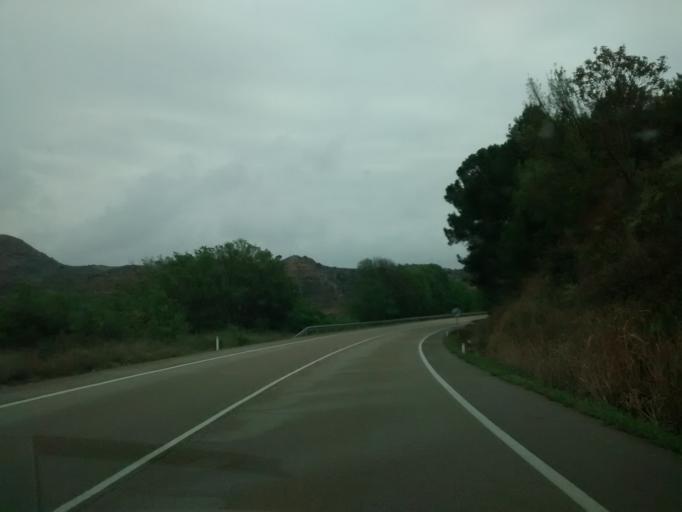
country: ES
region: Aragon
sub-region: Provincia de Zaragoza
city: Caspe
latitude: 41.2120
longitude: 0.0095
